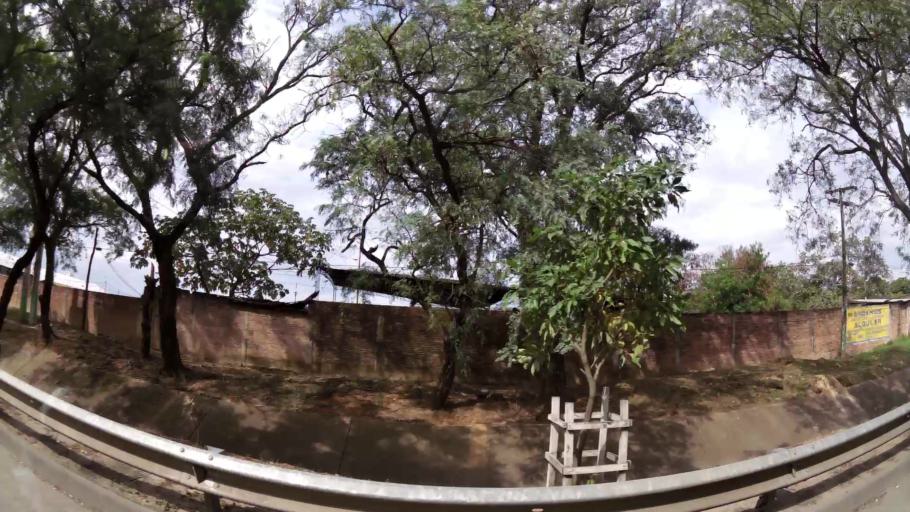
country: BO
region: Santa Cruz
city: Santa Cruz de la Sierra
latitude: -17.7845
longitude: -63.2063
